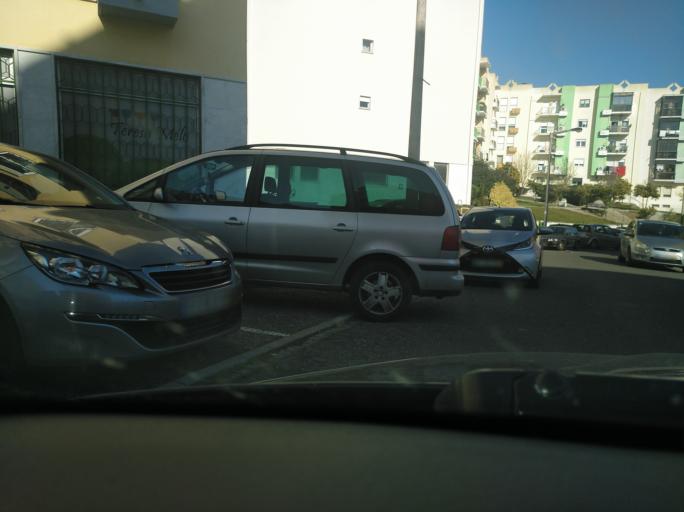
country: PT
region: Lisbon
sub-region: Odivelas
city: Famoes
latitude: 38.7804
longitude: -9.2108
